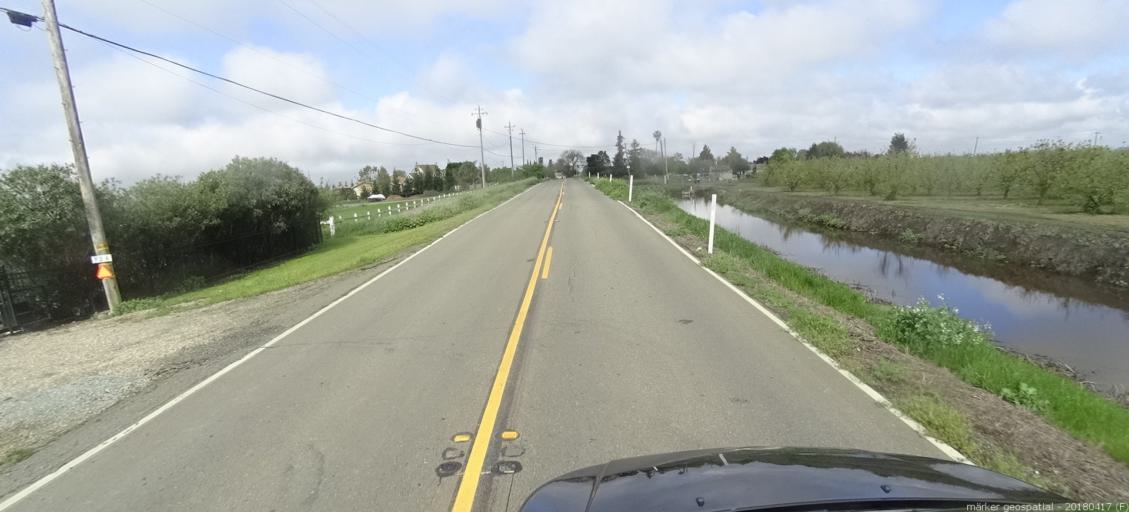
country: US
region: California
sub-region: Sacramento County
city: Walnut Grove
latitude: 38.2391
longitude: -121.5634
